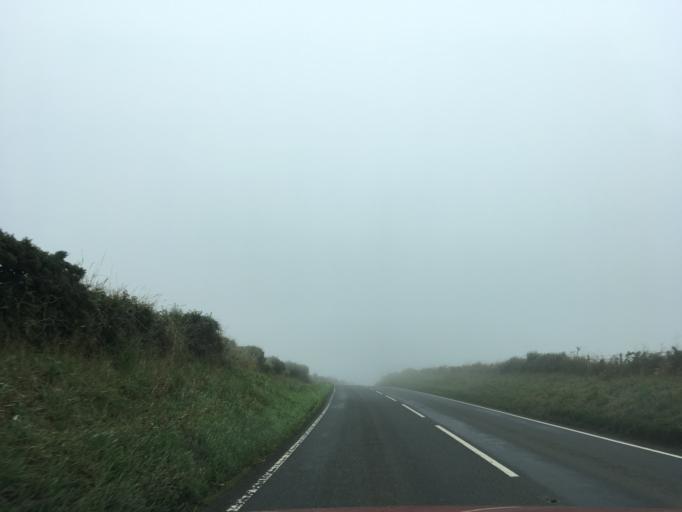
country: GB
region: Wales
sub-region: Pembrokeshire
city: Llanrhian
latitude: 51.8685
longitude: -5.1355
